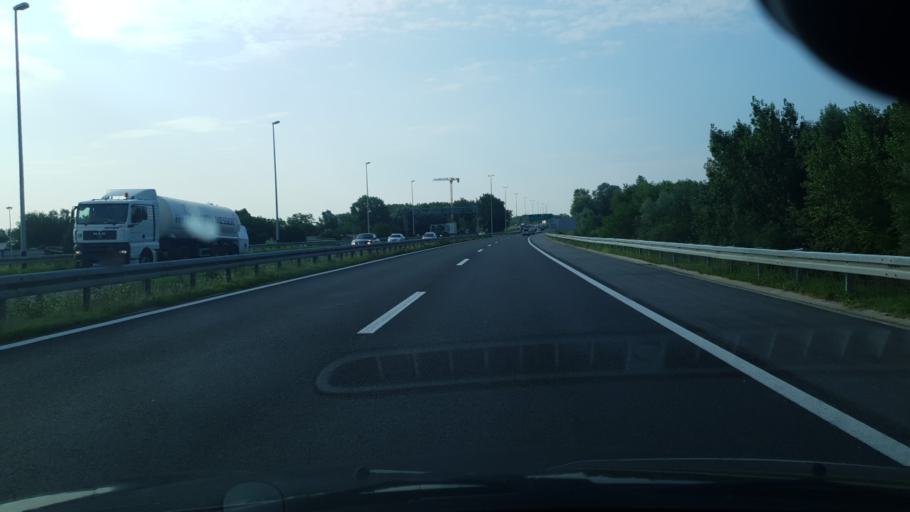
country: HR
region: Grad Zagreb
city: Jezdovec
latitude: 45.7957
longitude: 15.8452
